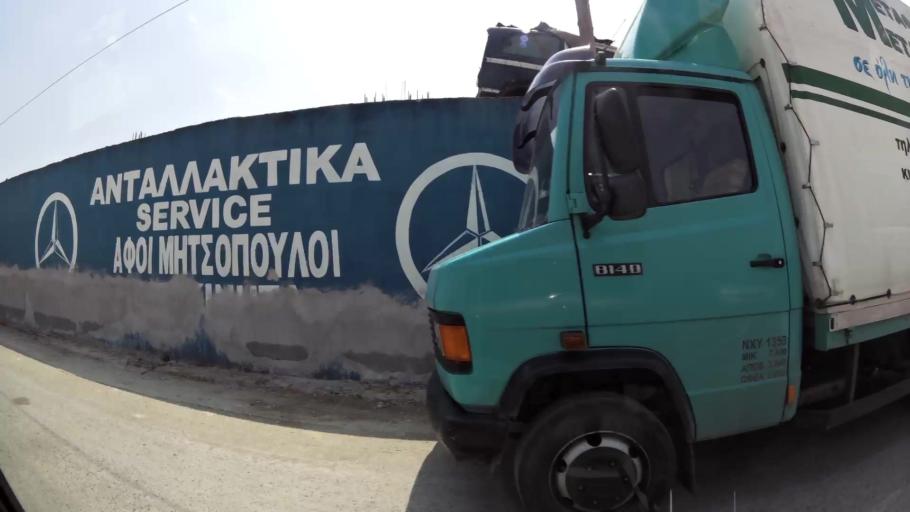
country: GR
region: Central Macedonia
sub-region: Nomos Thessalonikis
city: Menemeni
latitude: 40.6596
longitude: 22.8938
